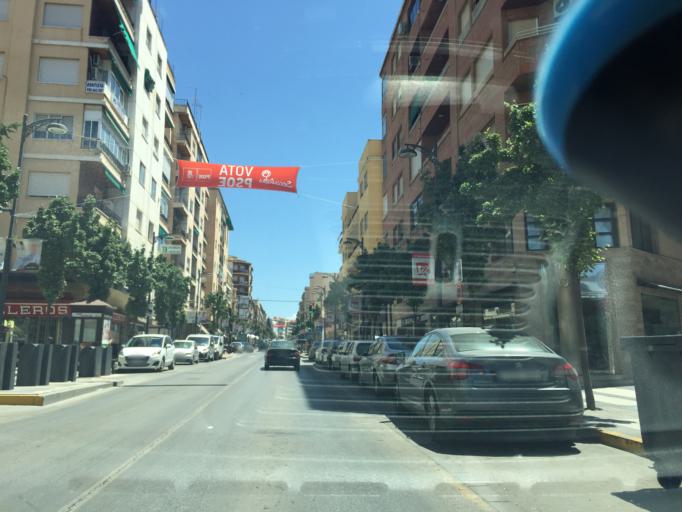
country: ES
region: Andalusia
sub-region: Provincia de Granada
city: Guadix
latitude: 37.3017
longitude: -3.1335
